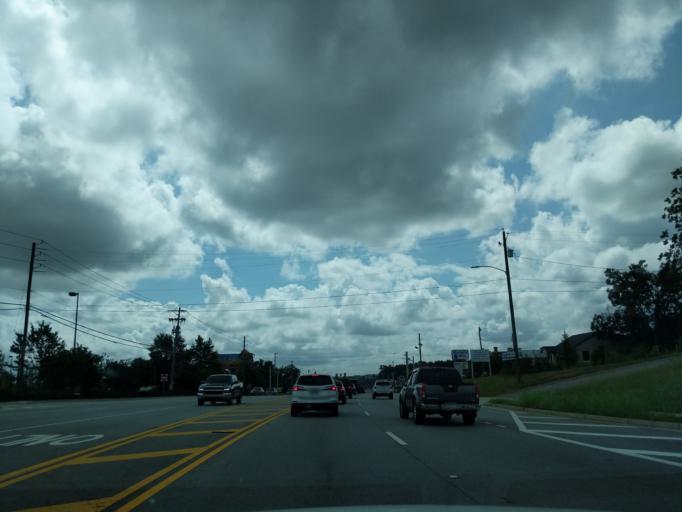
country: US
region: Georgia
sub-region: Columbia County
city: Evans
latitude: 33.5366
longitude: -82.1277
